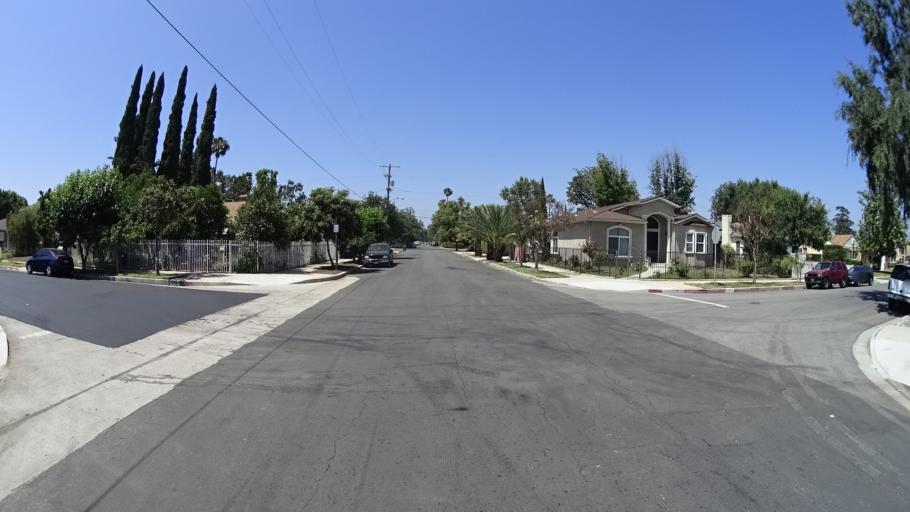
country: US
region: California
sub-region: Los Angeles County
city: Van Nuys
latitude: 34.1875
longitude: -118.4378
